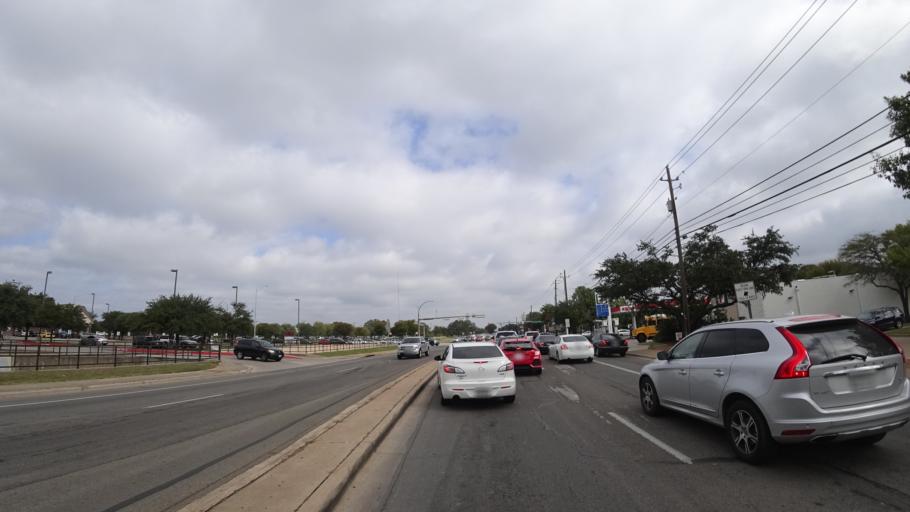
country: US
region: Texas
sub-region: Travis County
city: Shady Hollow
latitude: 30.2130
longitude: -97.8308
